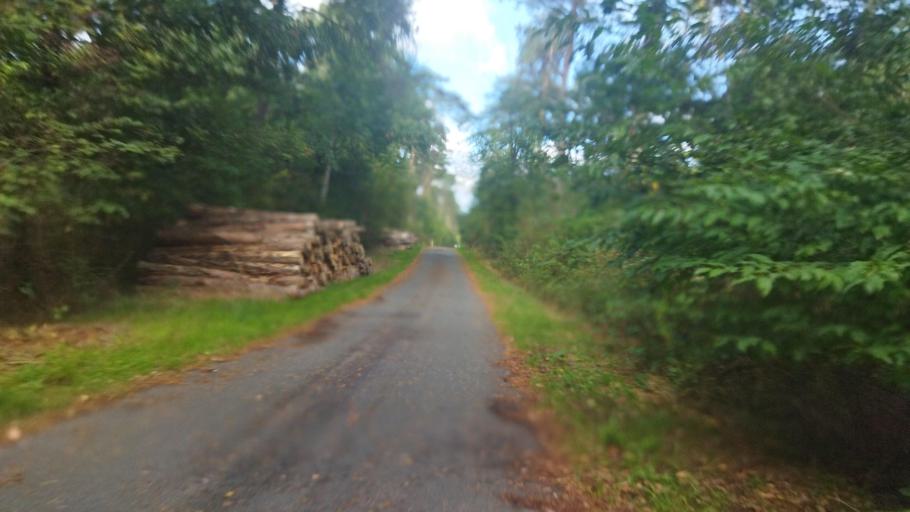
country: DE
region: North Rhine-Westphalia
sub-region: Regierungsbezirk Munster
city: Dulmen
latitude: 51.7908
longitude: 7.2564
